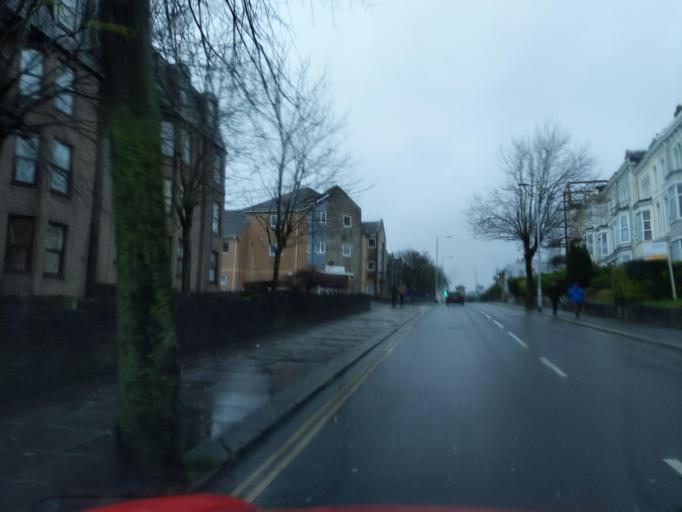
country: GB
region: England
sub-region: Plymouth
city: Plymouth
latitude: 50.3766
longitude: -4.1305
